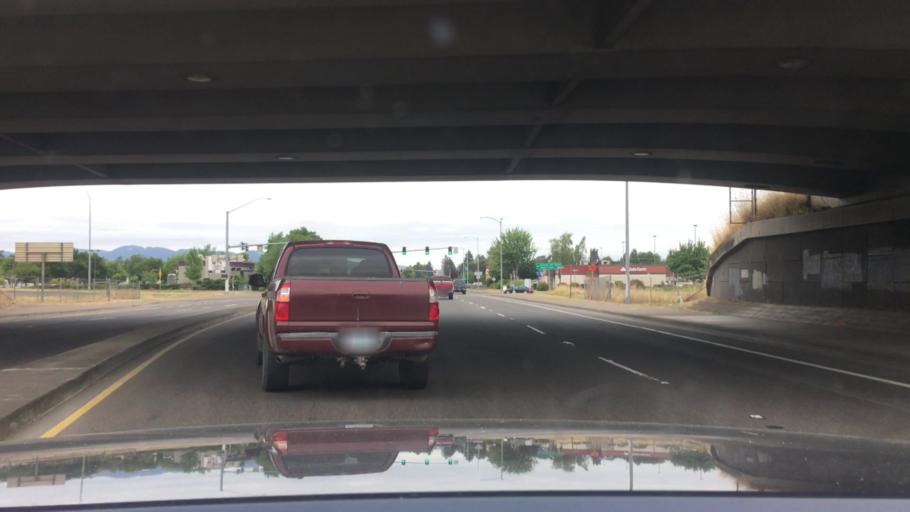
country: US
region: Oregon
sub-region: Lane County
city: Eugene
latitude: 44.0845
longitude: -123.1723
